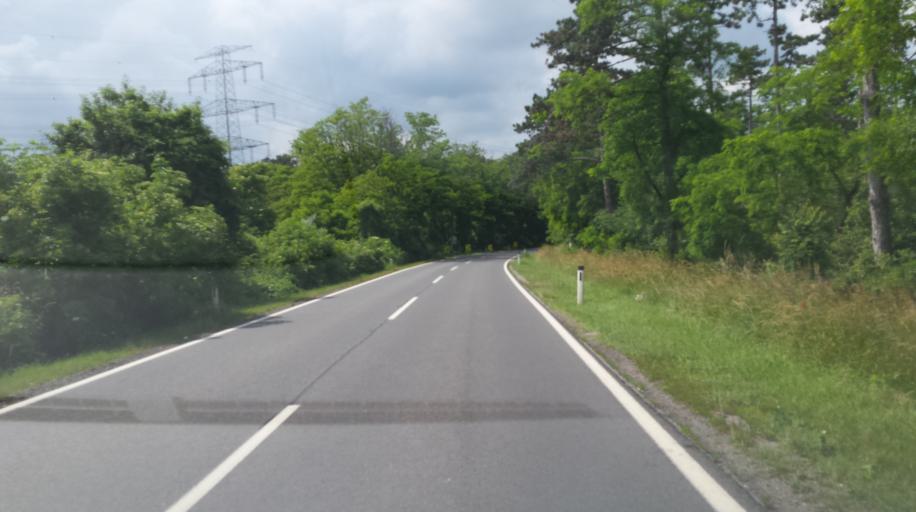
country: AT
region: Lower Austria
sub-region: Politischer Bezirk Ganserndorf
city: Aderklaa
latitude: 48.3046
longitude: 16.5423
